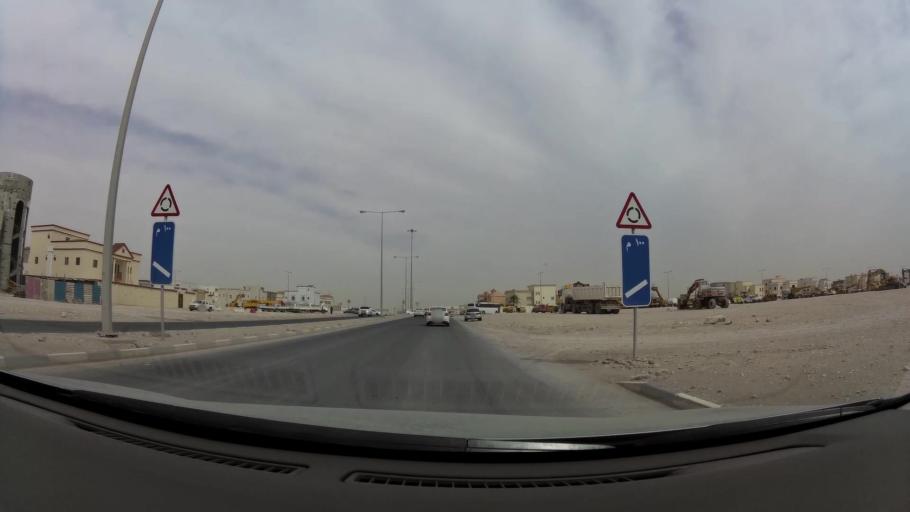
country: QA
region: Baladiyat ad Dawhah
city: Doha
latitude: 25.2117
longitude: 51.4826
